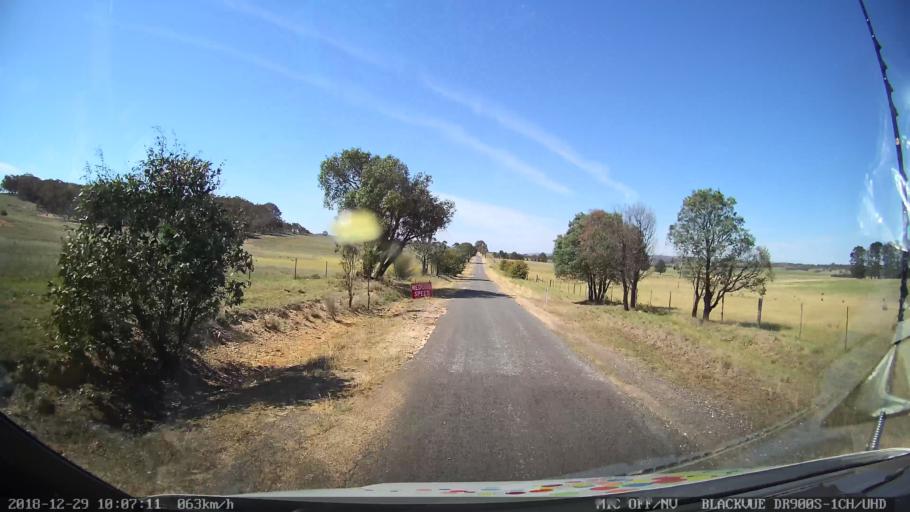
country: AU
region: New South Wales
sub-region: Yass Valley
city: Gundaroo
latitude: -34.8502
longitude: 149.4536
